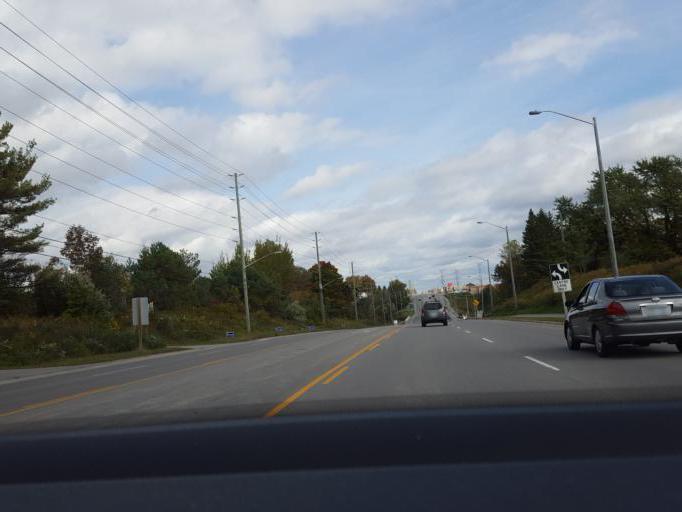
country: CA
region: Ontario
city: Ajax
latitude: 43.8904
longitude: -79.0634
